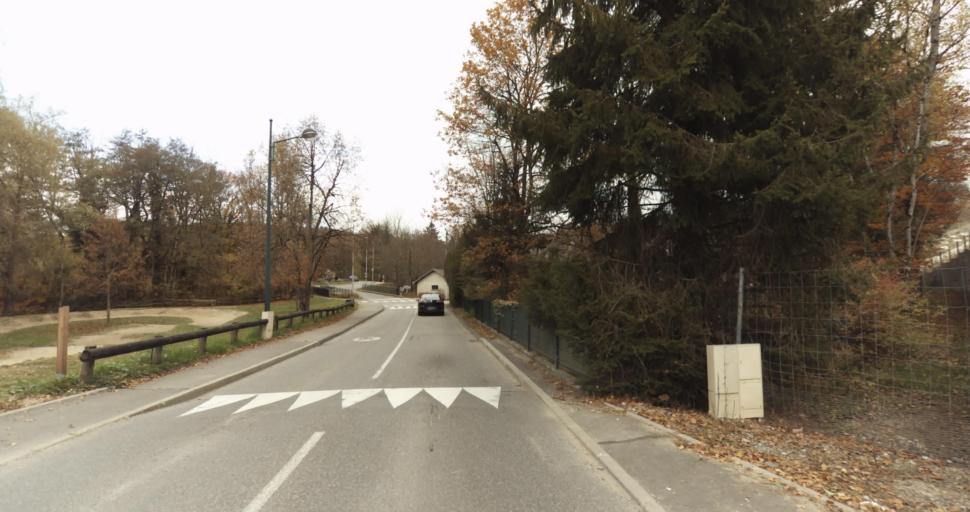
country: FR
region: Rhone-Alpes
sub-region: Departement de la Haute-Savoie
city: Pringy
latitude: 45.9513
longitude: 6.1159
